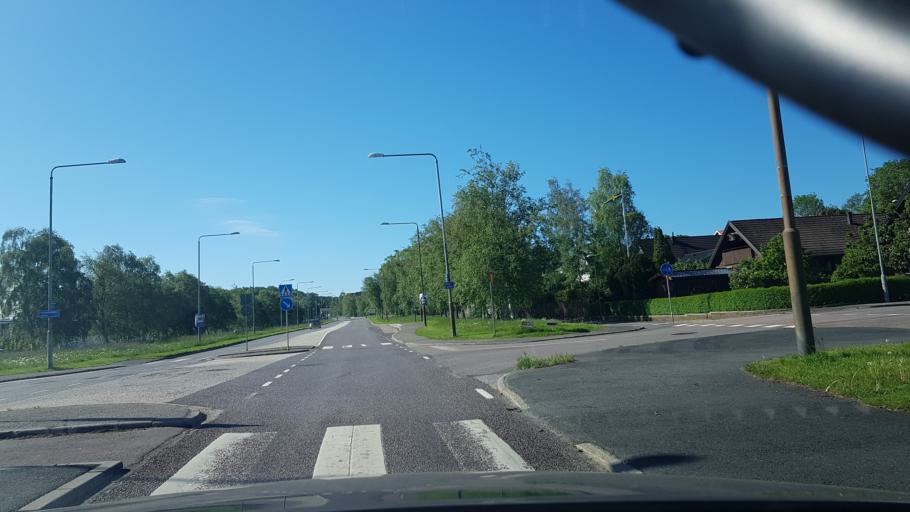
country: SE
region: Vaestra Goetaland
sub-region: Goteborg
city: Majorna
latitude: 57.6277
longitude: 11.9004
